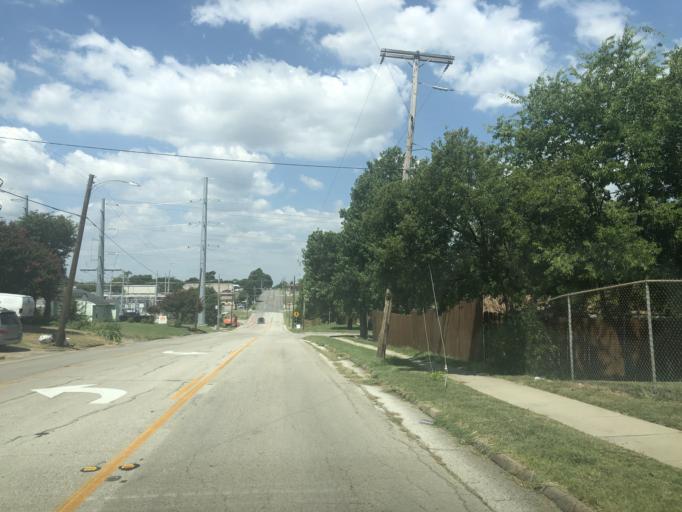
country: US
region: Texas
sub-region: Dallas County
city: Grand Prairie
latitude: 32.7447
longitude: -97.0329
